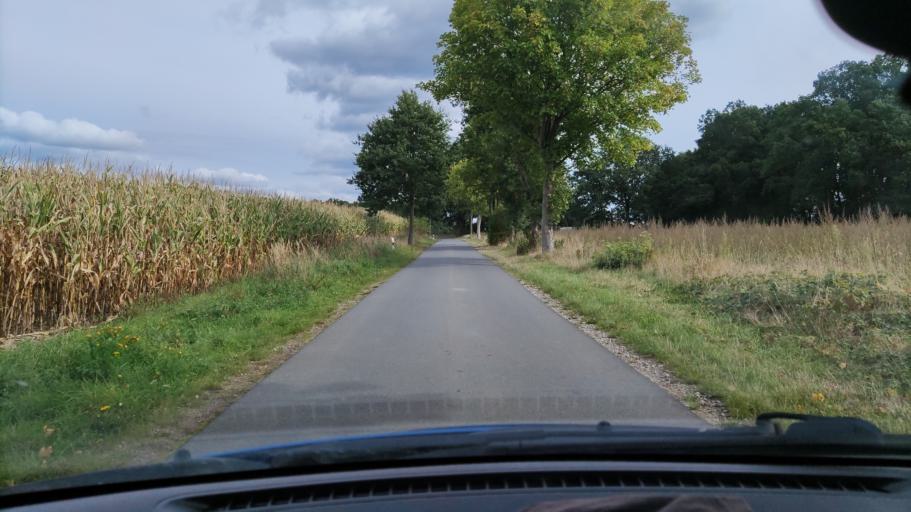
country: DE
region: Lower Saxony
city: Himbergen
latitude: 53.1094
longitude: 10.7032
